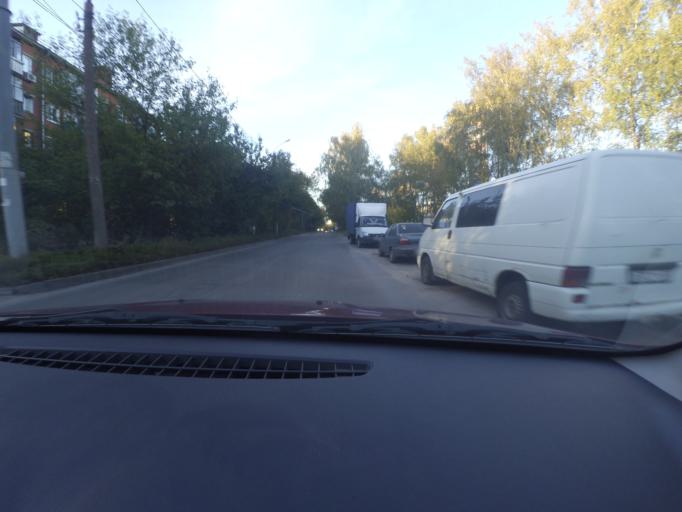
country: RU
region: Nizjnij Novgorod
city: Nizhniy Novgorod
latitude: 56.2859
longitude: 43.9942
